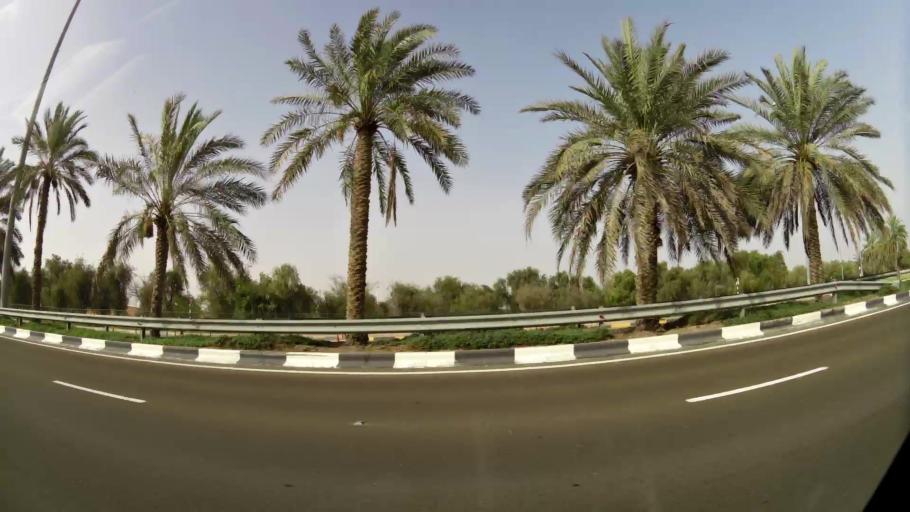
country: AE
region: Abu Dhabi
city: Al Ain
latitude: 24.1869
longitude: 55.5939
